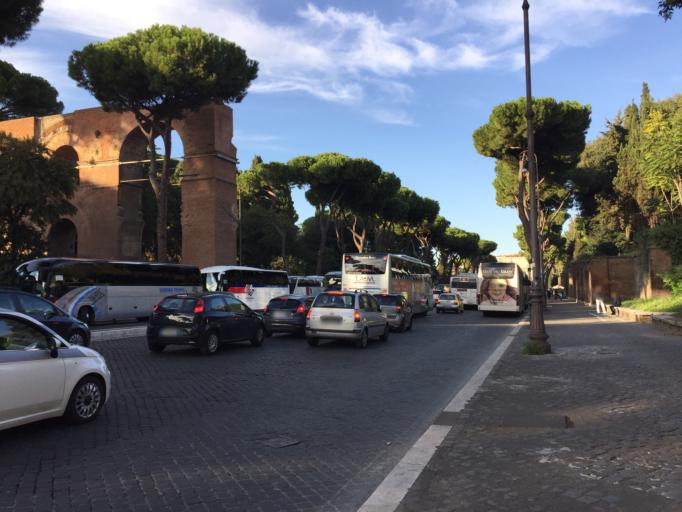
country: IT
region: Latium
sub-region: Citta metropolitana di Roma Capitale
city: Rome
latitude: 41.8866
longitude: 12.4899
